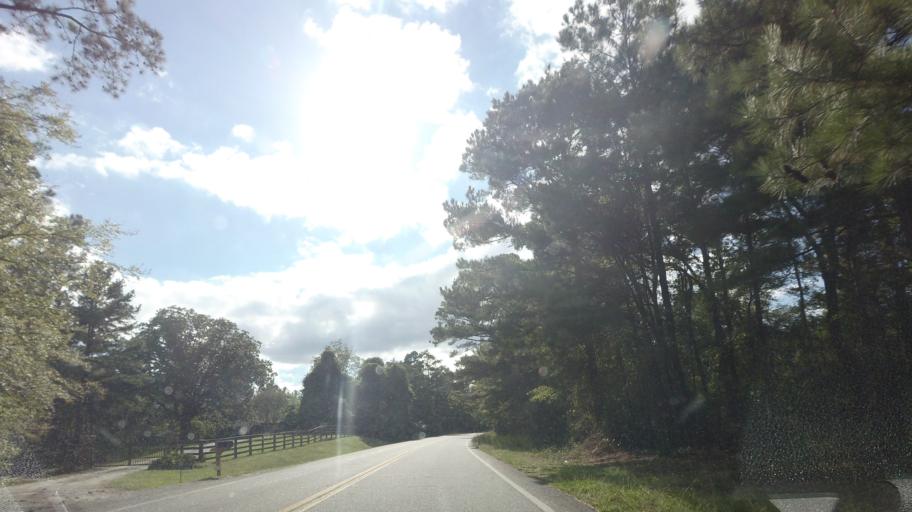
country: US
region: Georgia
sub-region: Monroe County
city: Forsyth
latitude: 33.0242
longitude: -83.7664
